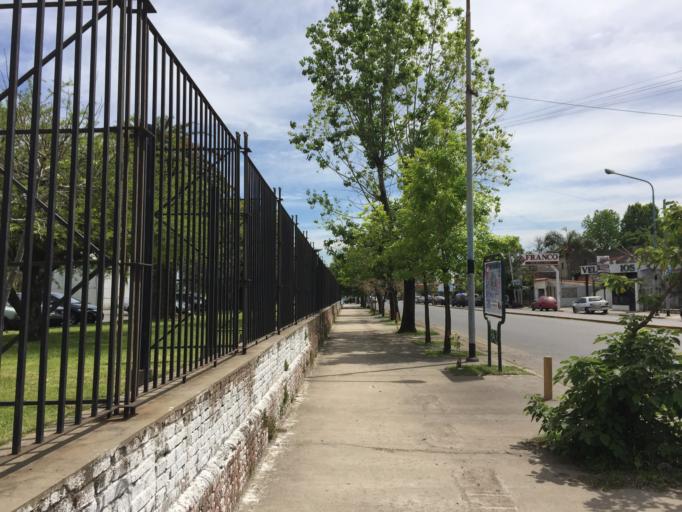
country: AR
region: Buenos Aires
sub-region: Partido de Lomas de Zamora
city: Lomas de Zamora
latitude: -34.7354
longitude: -58.3903
